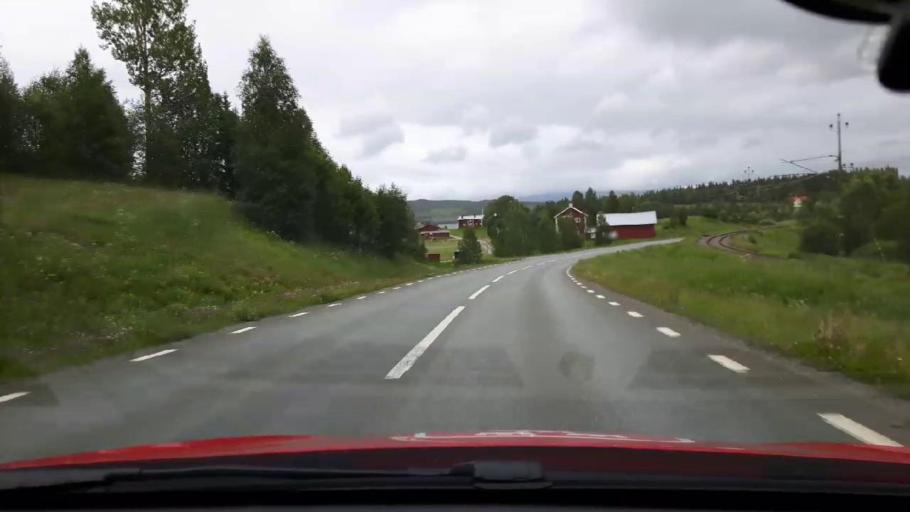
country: SE
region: Jaemtland
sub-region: Are Kommun
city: Are
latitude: 63.3636
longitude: 12.6256
